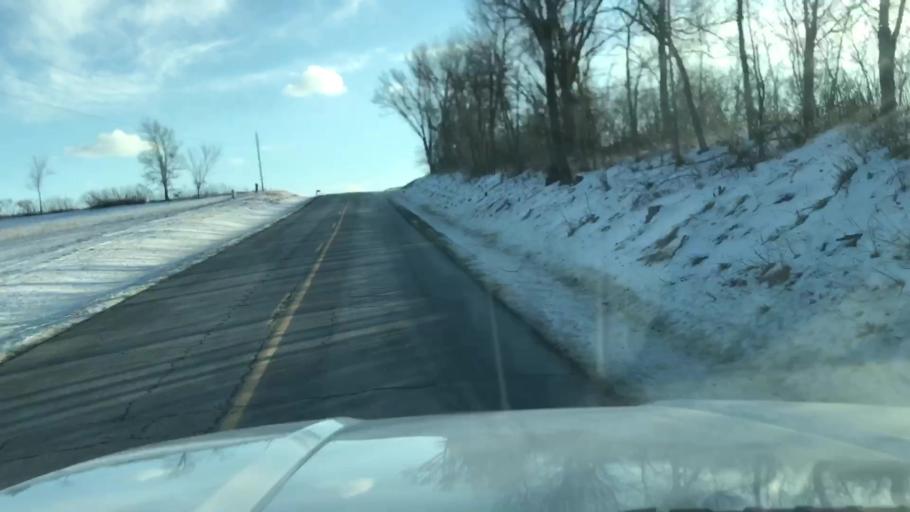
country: US
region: Missouri
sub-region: Holt County
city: Oregon
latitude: 40.0653
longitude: -94.9748
